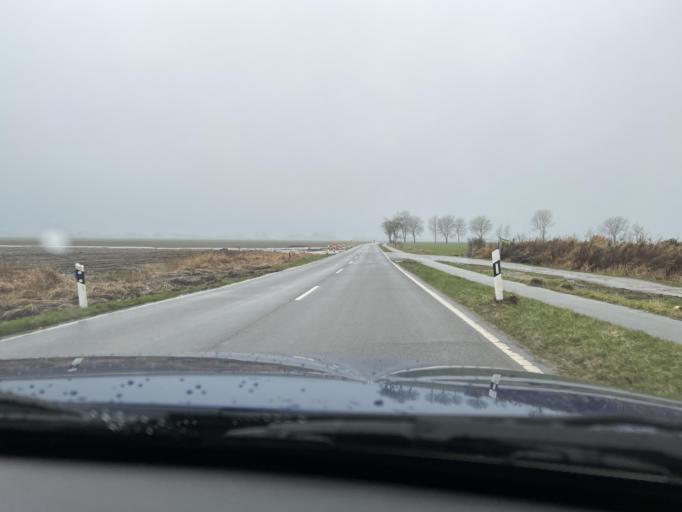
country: DE
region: Schleswig-Holstein
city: Stelle-Wittenwurth
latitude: 54.2430
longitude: 9.0351
